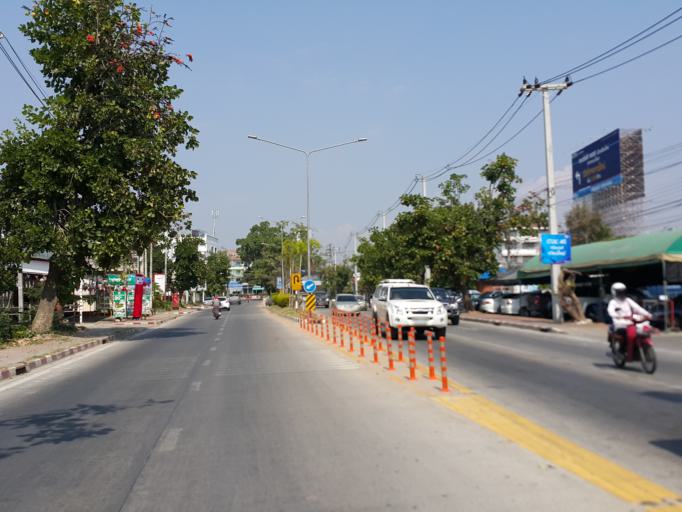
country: TH
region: Chiang Mai
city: Chiang Mai
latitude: 18.8089
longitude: 98.9952
